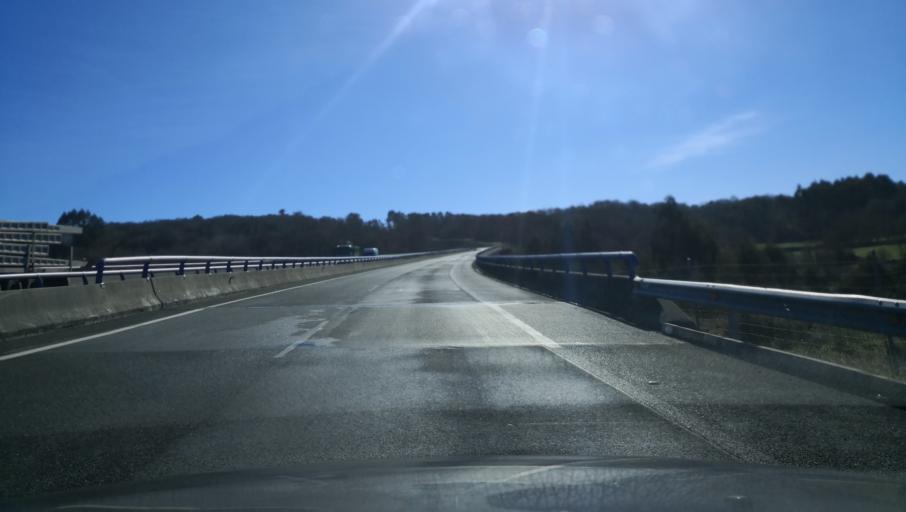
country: ES
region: Galicia
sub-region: Provincia de Pontevedra
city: Lalin
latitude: 42.6298
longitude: -8.1197
